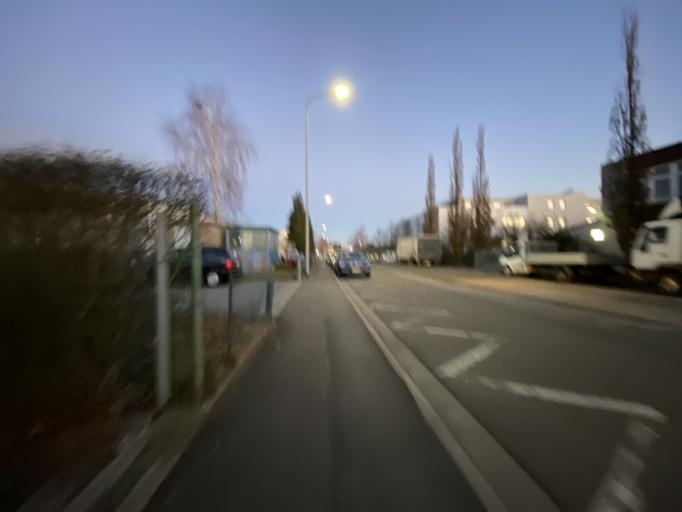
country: DE
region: Hesse
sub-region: Regierungsbezirk Darmstadt
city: Hochheim am Main
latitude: 50.0705
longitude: 8.3838
